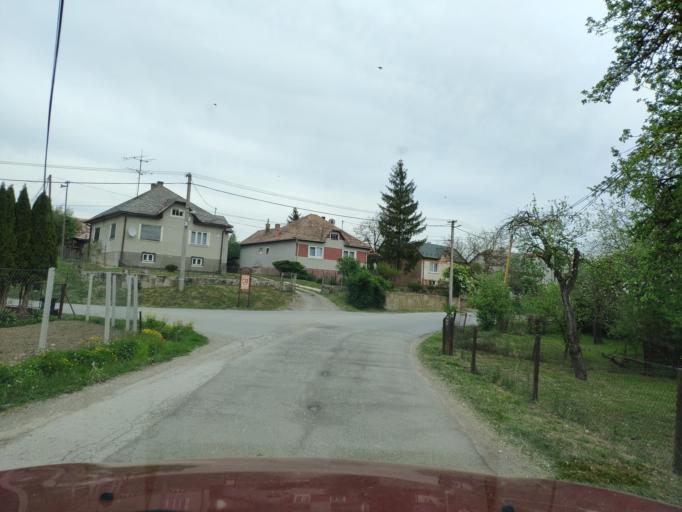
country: SK
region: Banskobystricky
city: Revuca
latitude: 48.5025
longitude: 20.1986
